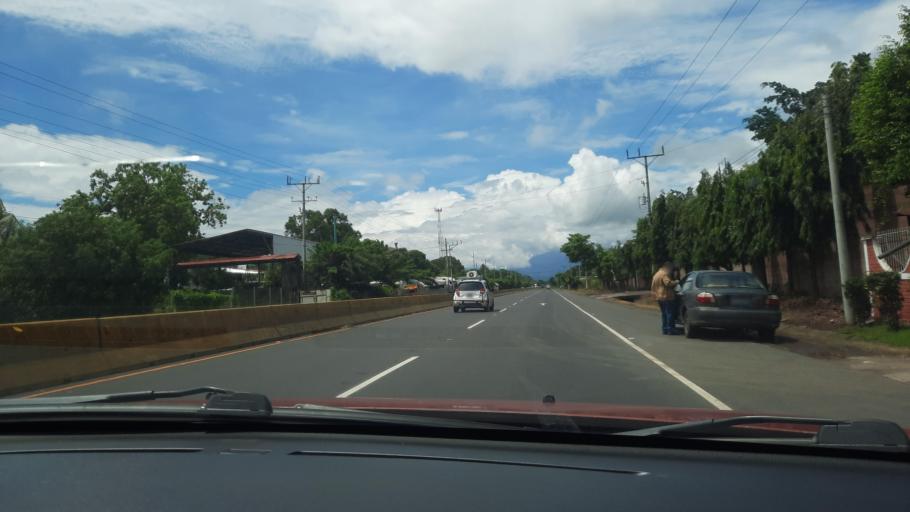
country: SV
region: Sonsonate
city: Acajutla
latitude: 13.6315
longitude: -89.7831
